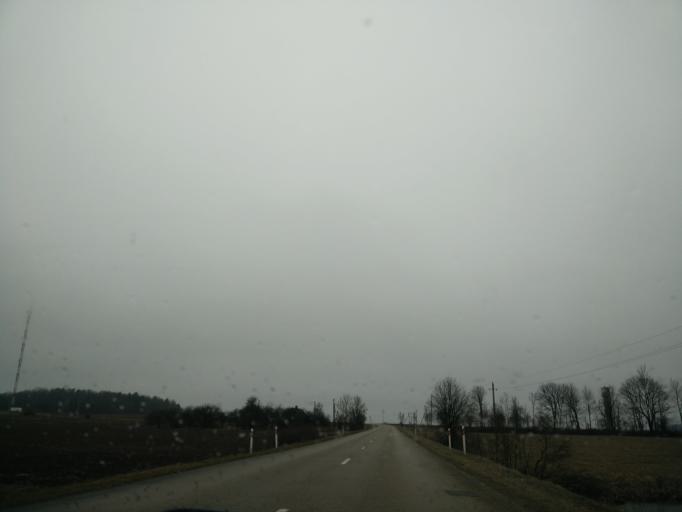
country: LT
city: Ariogala
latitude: 55.3452
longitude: 23.3919
